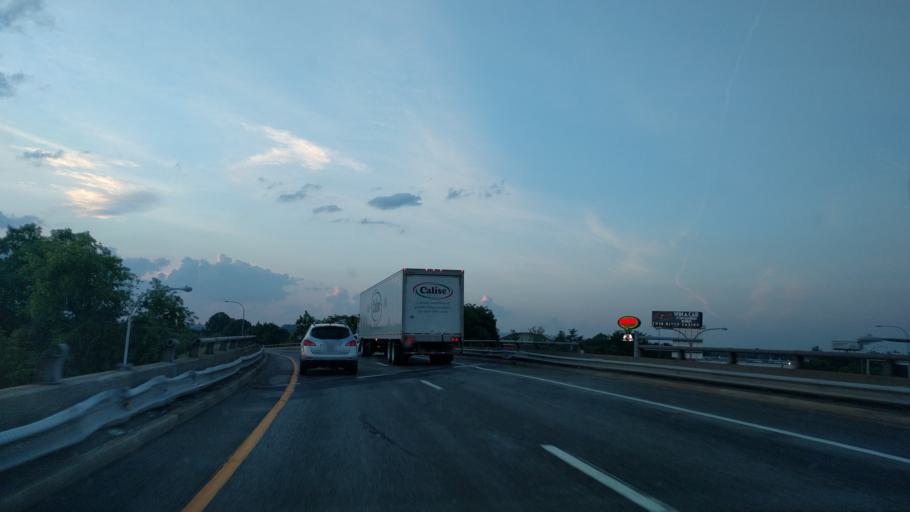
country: US
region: Rhode Island
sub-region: Providence County
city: Providence
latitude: 41.8357
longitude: -71.4154
